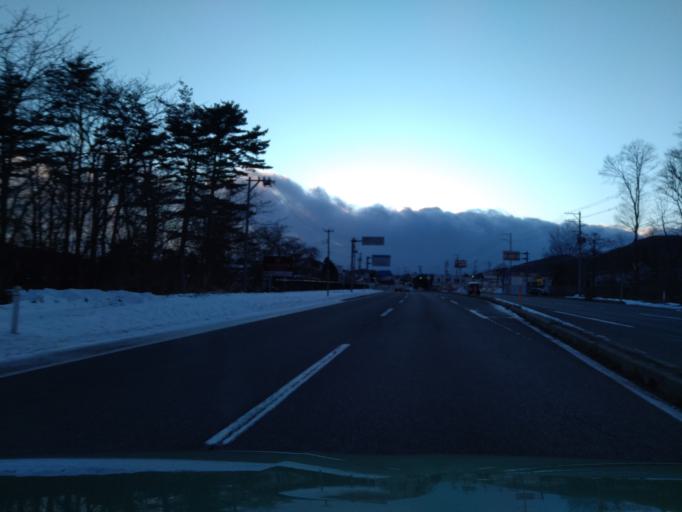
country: JP
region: Iwate
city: Shizukuishi
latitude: 39.6991
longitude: 141.0250
